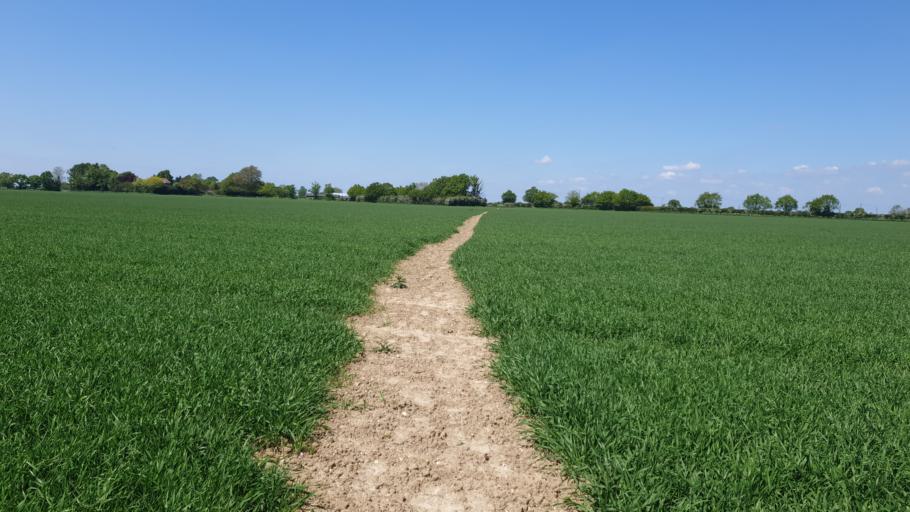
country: GB
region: England
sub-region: Essex
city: Manningtree
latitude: 51.9090
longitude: 1.0514
